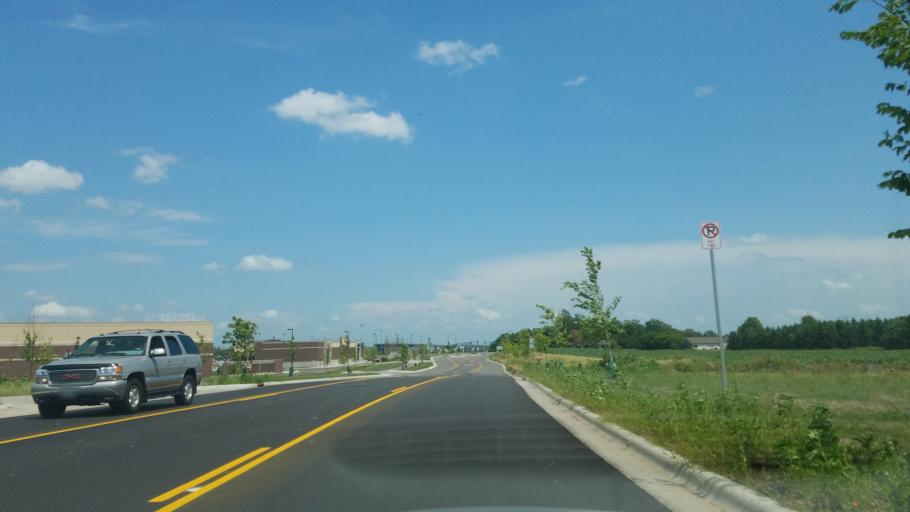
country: US
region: Minnesota
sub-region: Washington County
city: Woodbury
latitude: 44.8873
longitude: -92.9496
